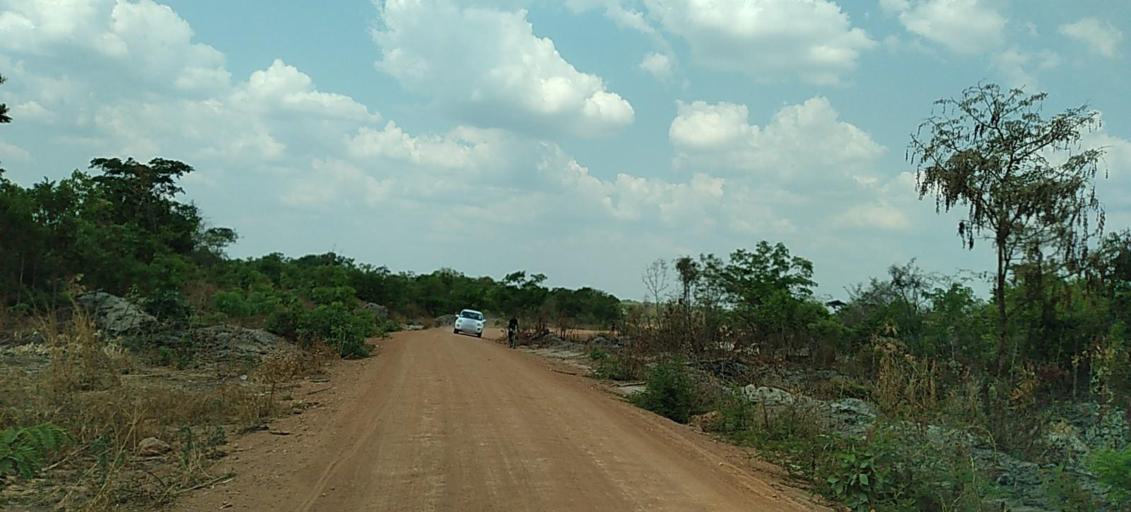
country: ZM
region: Copperbelt
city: Luanshya
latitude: -13.1386
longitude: 28.3385
